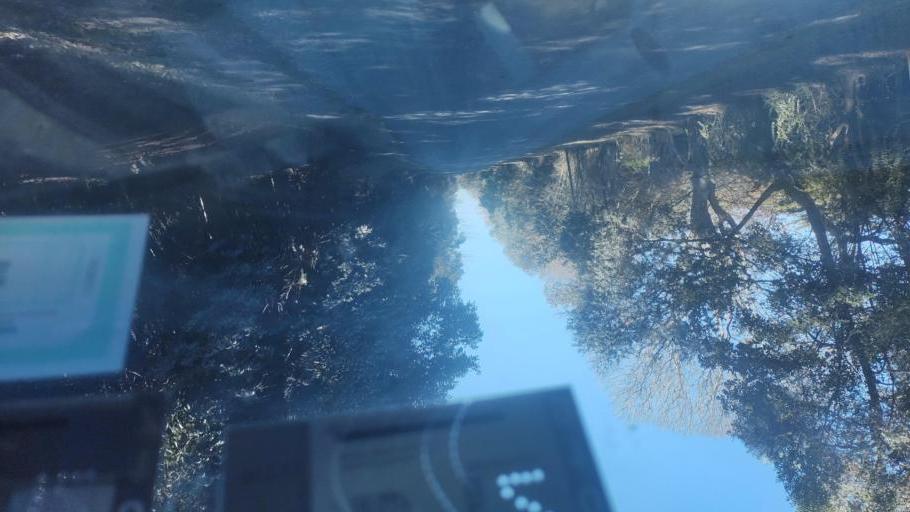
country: AR
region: Buenos Aires
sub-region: Partido de La Plata
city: La Plata
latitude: -34.8512
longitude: -58.1035
